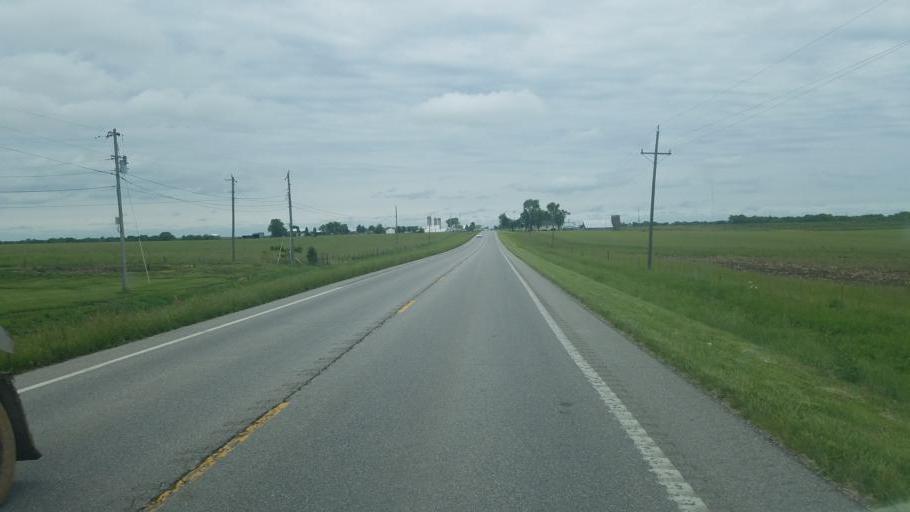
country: US
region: Missouri
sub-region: Morgan County
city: Versailles
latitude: 38.4713
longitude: -92.8088
